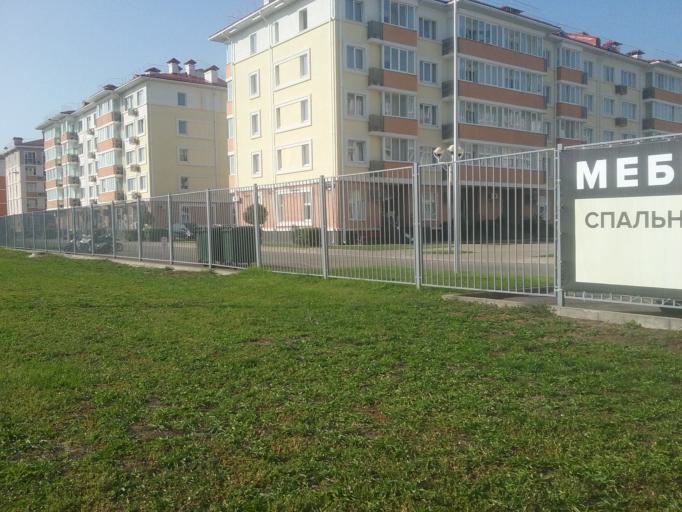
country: RU
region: Krasnodarskiy
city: Adler
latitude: 43.3998
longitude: 39.9802
